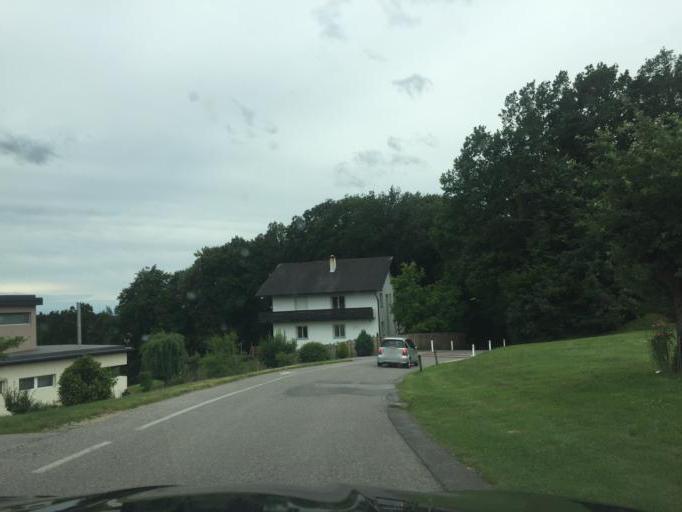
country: AT
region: Styria
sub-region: Politischer Bezirk Graz-Umgebung
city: Hart bei Graz
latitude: 47.0562
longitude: 15.5136
